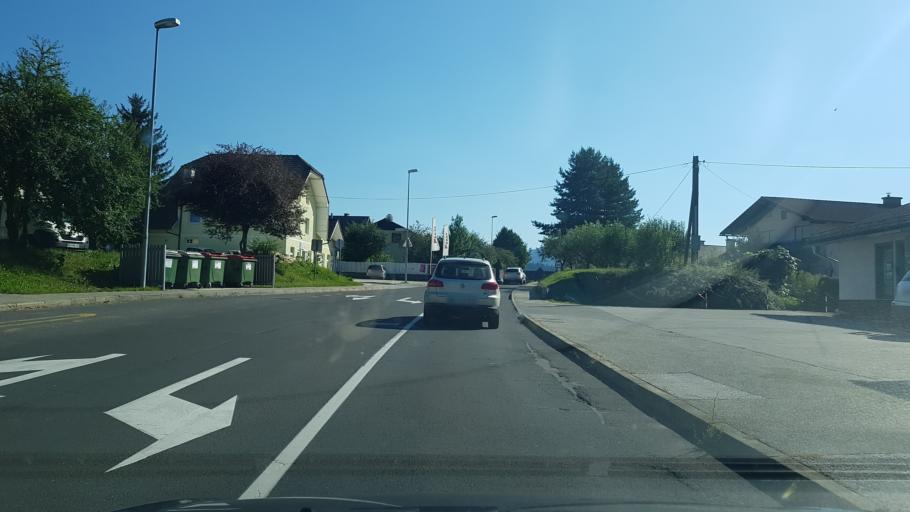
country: SI
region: Slovenj Gradec
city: Slovenj Gradec
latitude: 46.5043
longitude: 15.0747
